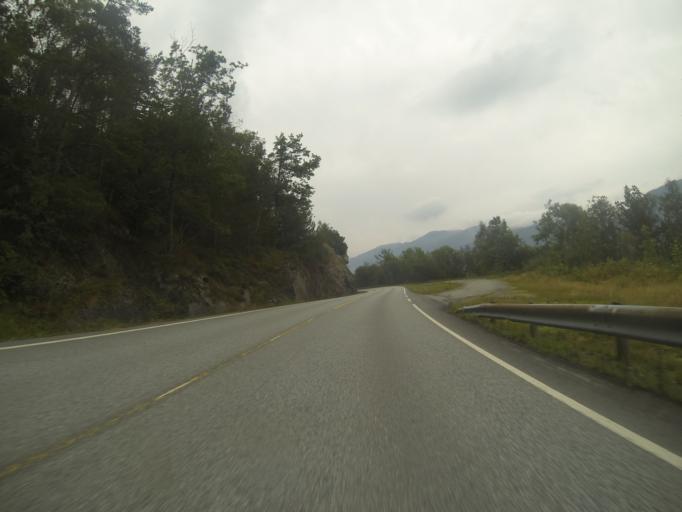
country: NO
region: Rogaland
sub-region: Suldal
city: Sand
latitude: 59.5600
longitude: 6.2668
